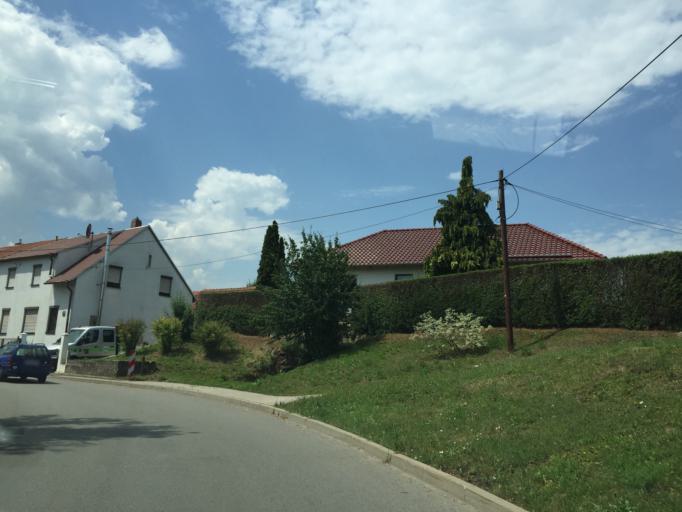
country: DE
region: Thuringia
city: Alkersleben
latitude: 50.8245
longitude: 11.0167
